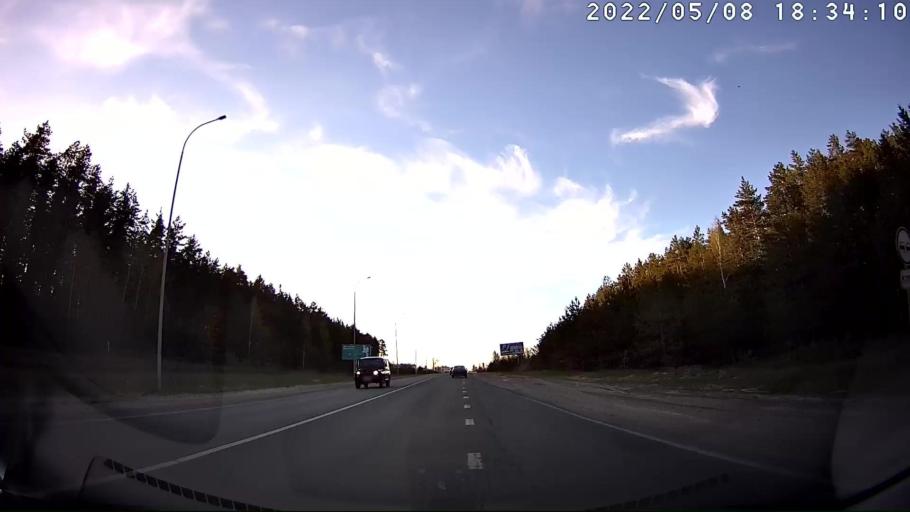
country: RU
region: Mariy-El
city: Volzhsk
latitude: 55.8977
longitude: 48.3564
